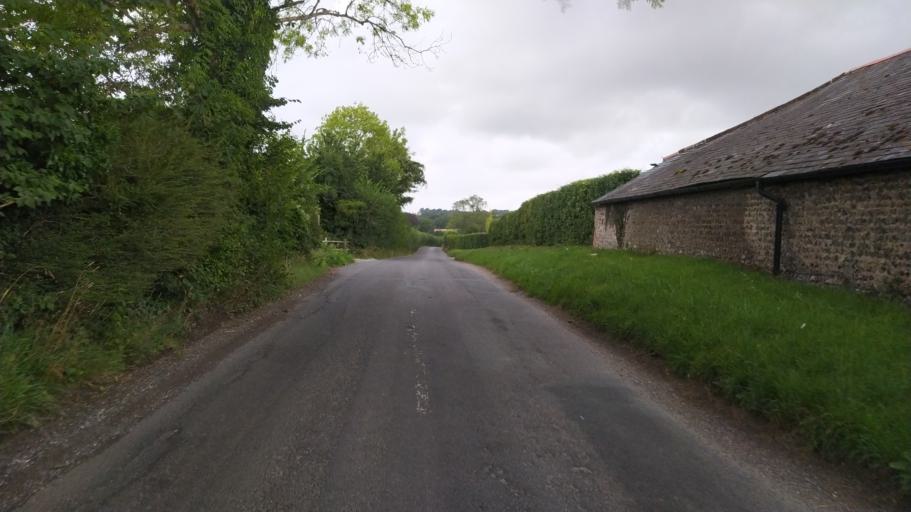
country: GB
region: England
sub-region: Hampshire
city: Four Marks
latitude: 51.0087
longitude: -1.0543
